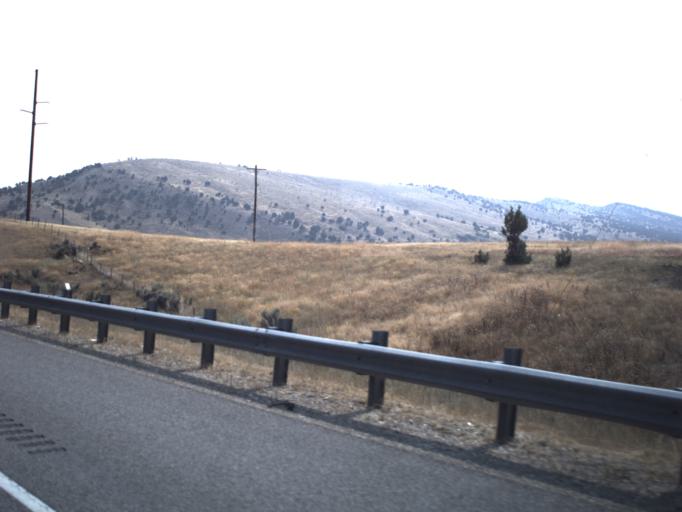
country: US
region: Utah
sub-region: Summit County
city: Coalville
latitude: 40.9485
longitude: -111.4201
